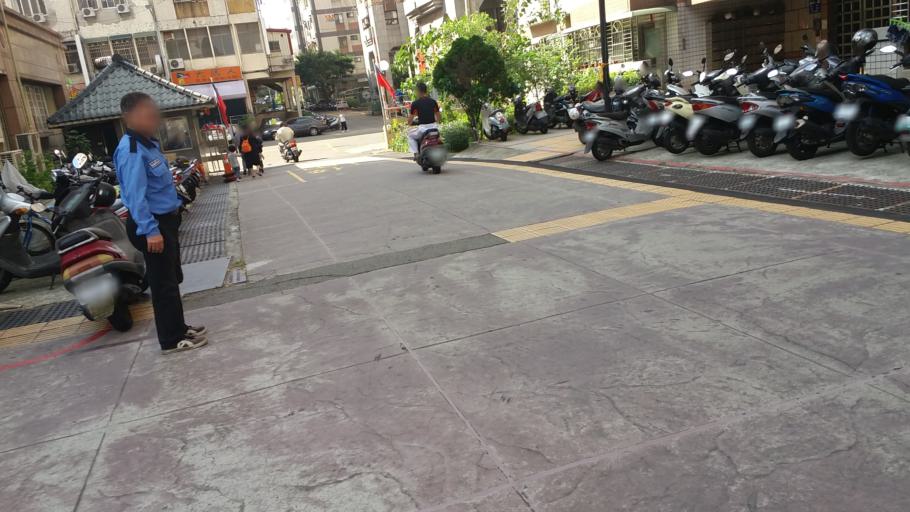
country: TW
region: Taiwan
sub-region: Hsinchu
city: Hsinchu
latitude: 24.8010
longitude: 120.9942
